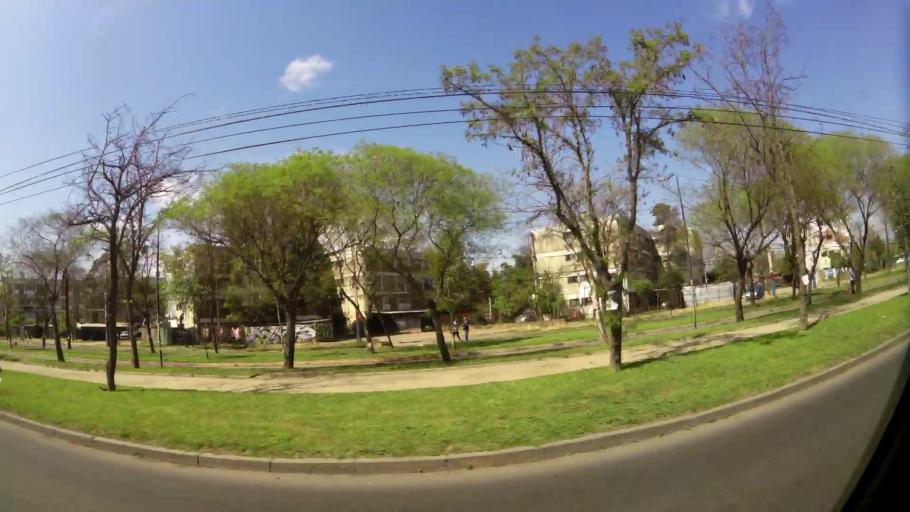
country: CL
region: Santiago Metropolitan
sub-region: Provincia de Santiago
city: Lo Prado
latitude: -33.4703
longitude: -70.7177
